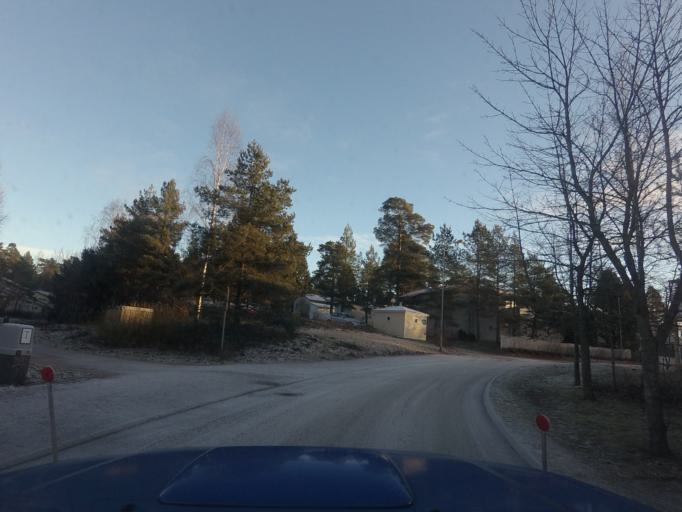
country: FI
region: Uusimaa
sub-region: Helsinki
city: Espoo
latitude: 60.2054
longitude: 24.6264
